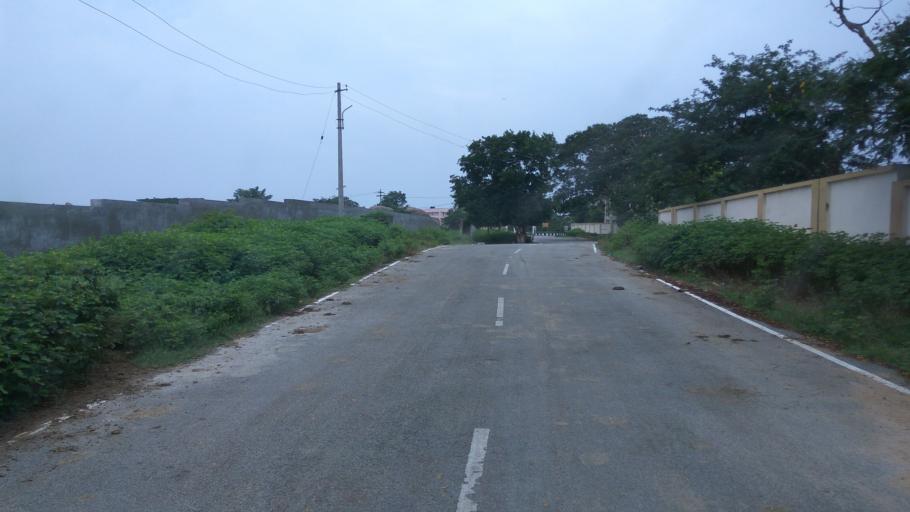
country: IN
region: Telangana
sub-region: Rangareddi
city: Ghatkesar
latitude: 17.5329
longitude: 78.6903
